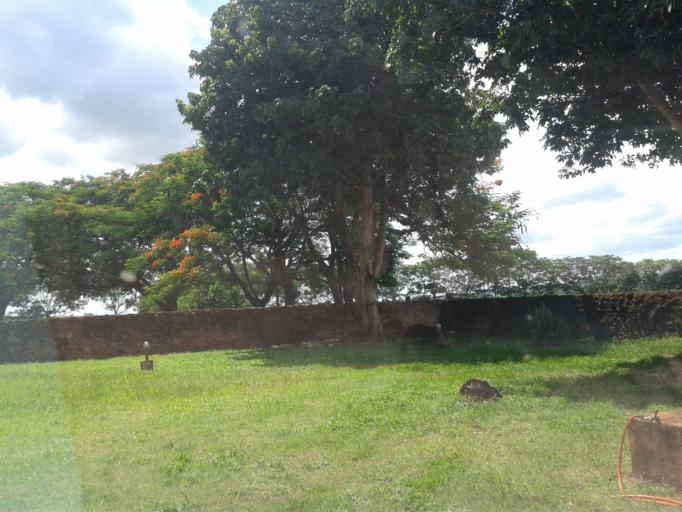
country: BR
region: Minas Gerais
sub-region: Santa Vitoria
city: Santa Vitoria
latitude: -19.1420
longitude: -50.6263
